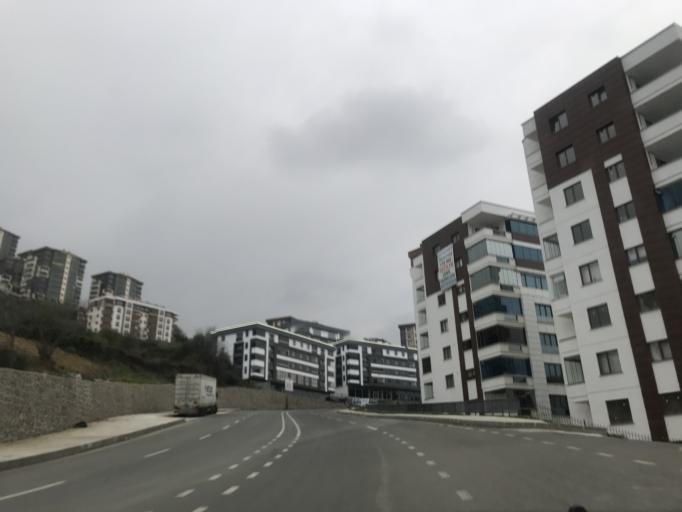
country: TR
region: Trabzon
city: Akcaabat
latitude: 41.0050
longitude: 39.6246
